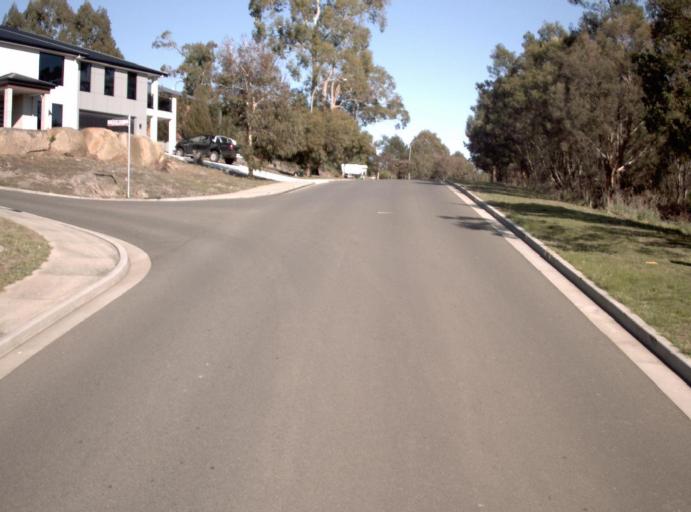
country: AU
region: Tasmania
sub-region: Launceston
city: Summerhill
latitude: -41.4739
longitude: 147.1549
